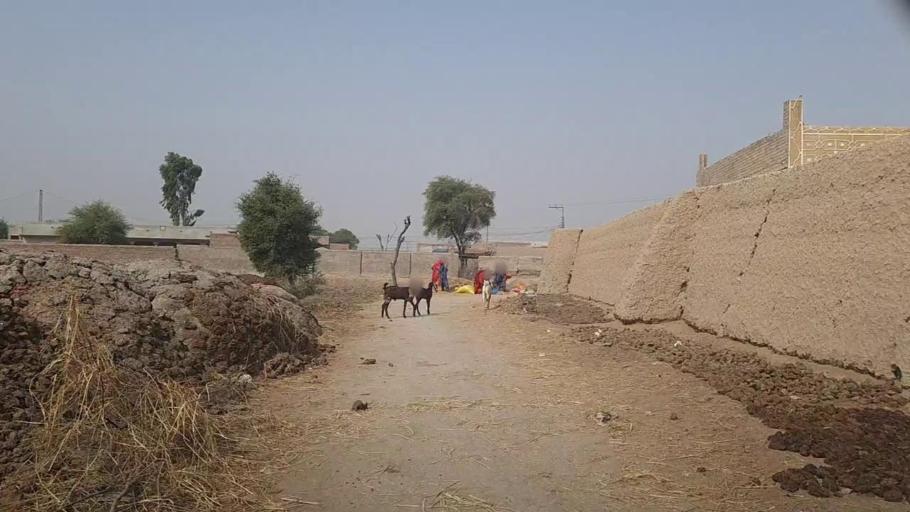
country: PK
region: Sindh
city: Kashmor
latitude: 28.4586
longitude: 69.5503
